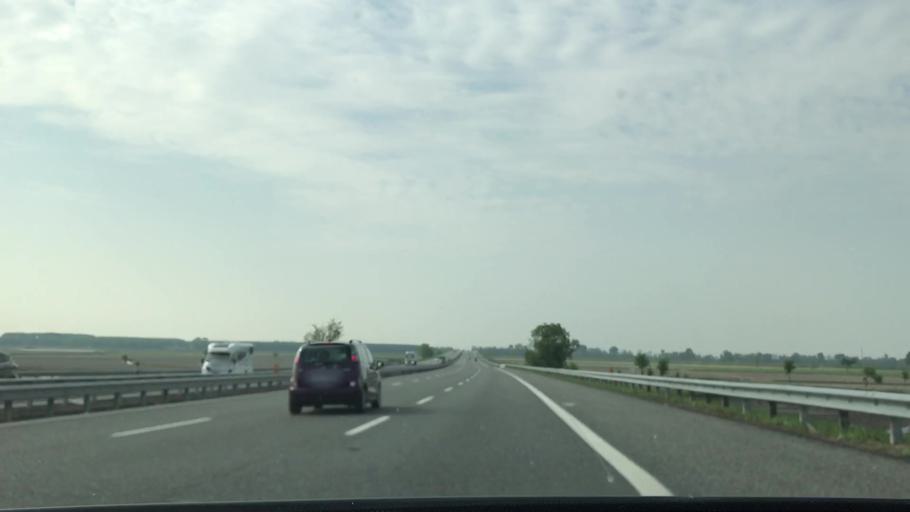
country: IT
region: Piedmont
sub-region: Provincia di Vercelli
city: Borgo Vercelli
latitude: 45.3239
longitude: 8.4698
